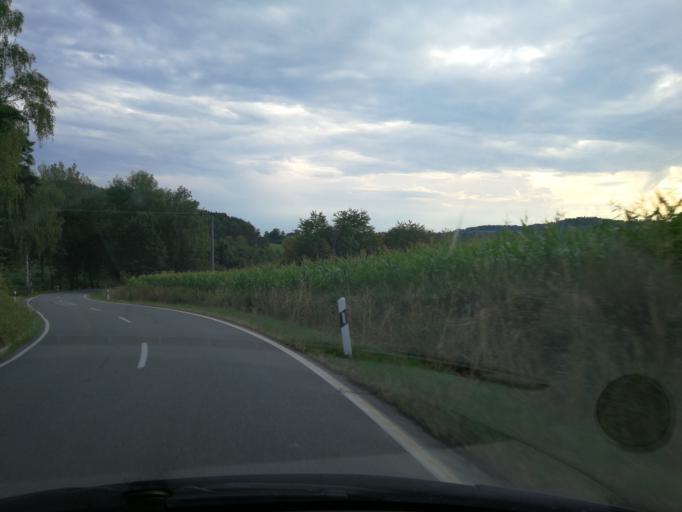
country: DE
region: Bavaria
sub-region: Lower Bavaria
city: Haibach
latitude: 49.0328
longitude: 12.7195
